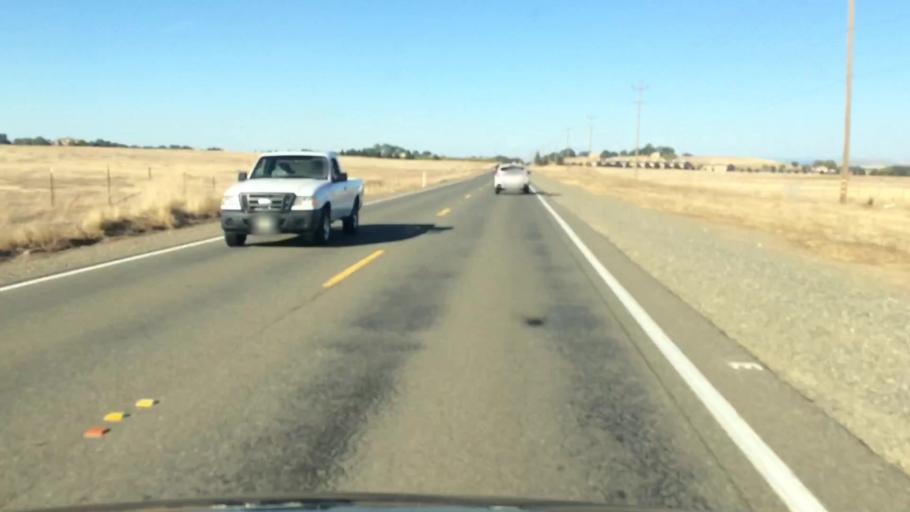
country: US
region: California
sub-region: Sacramento County
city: Rancho Murieta
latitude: 38.4773
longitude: -121.1695
